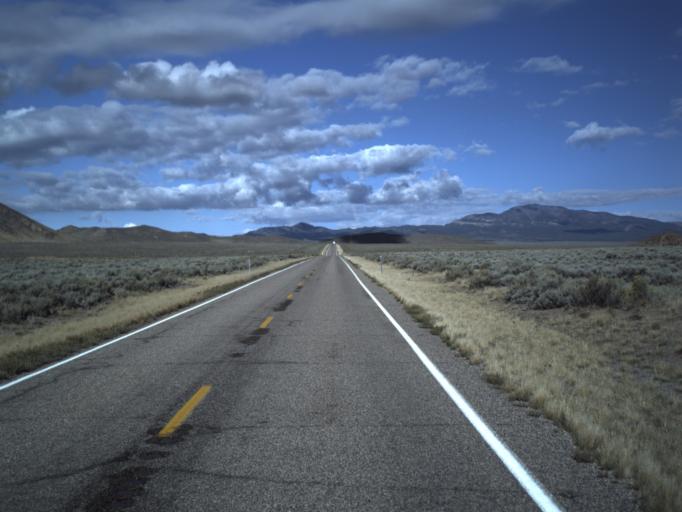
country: US
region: Utah
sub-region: Beaver County
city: Milford
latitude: 38.4152
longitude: -113.0804
